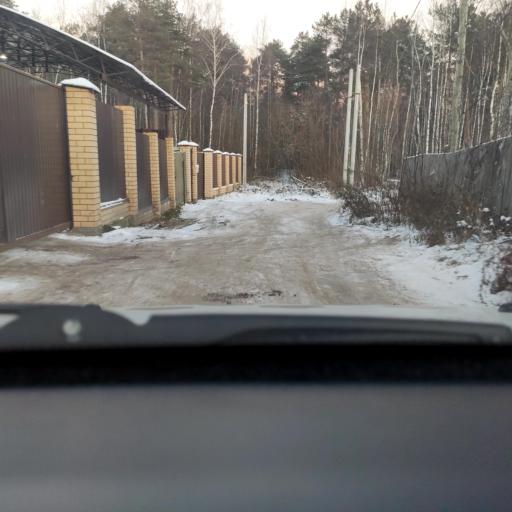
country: RU
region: Perm
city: Perm
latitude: 58.0352
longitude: 56.2525
